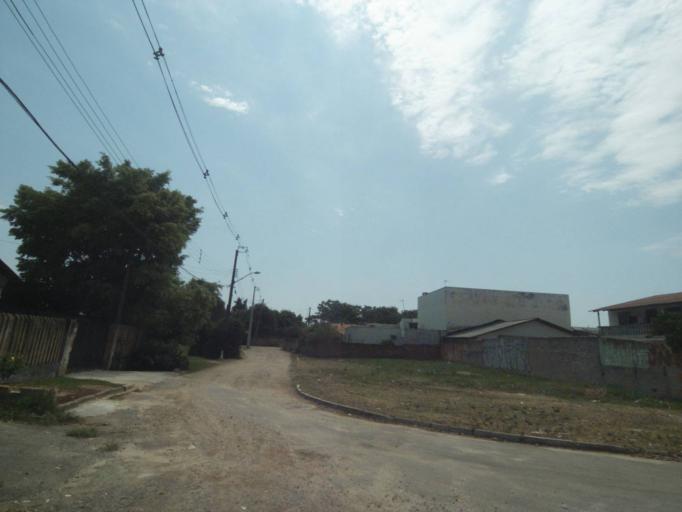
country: BR
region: Parana
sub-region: Sao Jose Dos Pinhais
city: Sao Jose dos Pinhais
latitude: -25.5242
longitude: -49.2666
